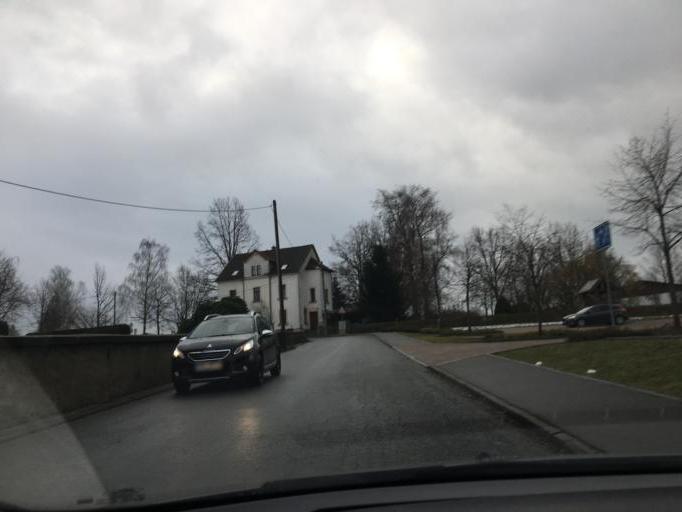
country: DE
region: Saxony
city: Pfaffroda
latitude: 50.8919
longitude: 12.5371
